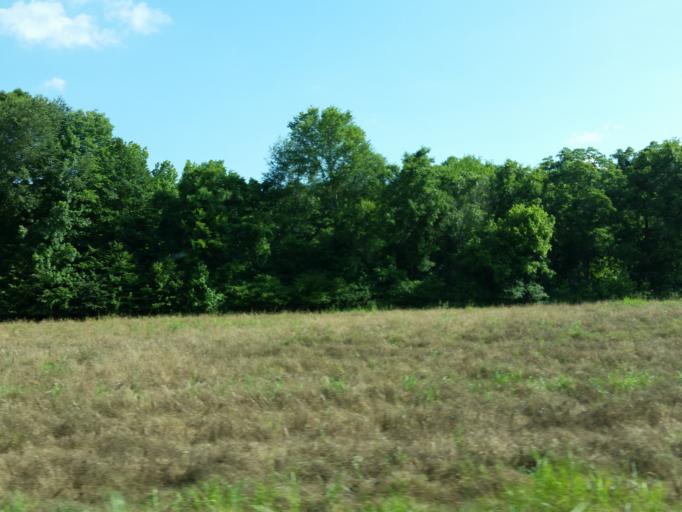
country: US
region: Tennessee
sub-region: Perry County
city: Linden
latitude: 35.6353
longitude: -87.7835
